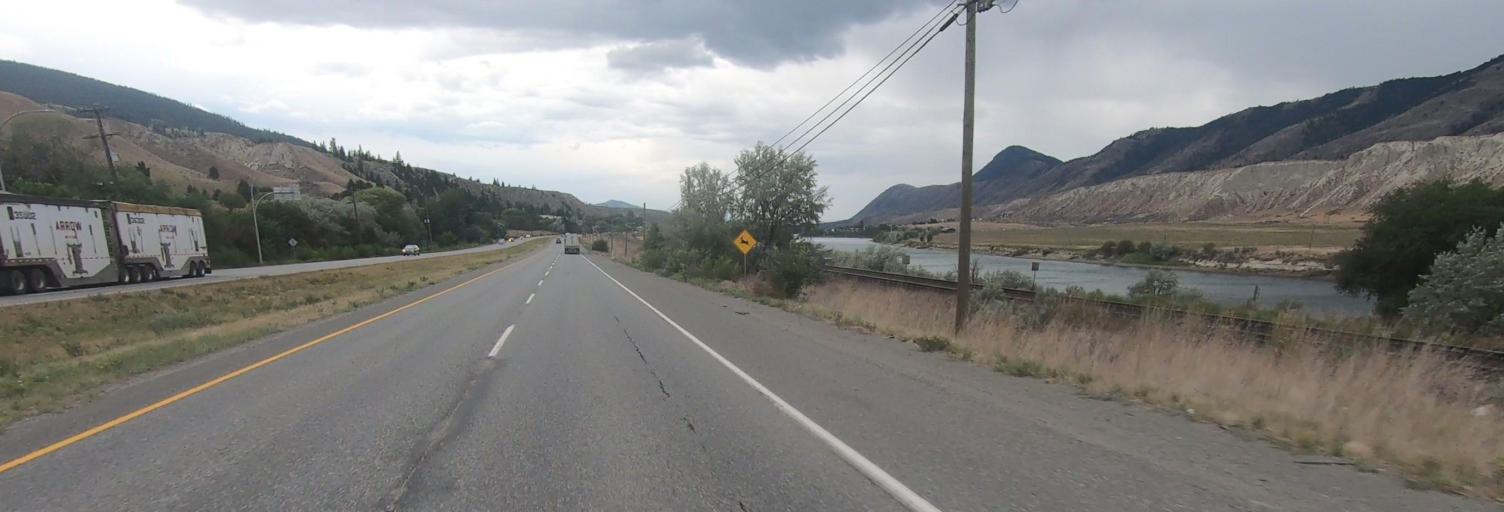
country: CA
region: British Columbia
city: Kamloops
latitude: 50.6695
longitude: -120.1890
